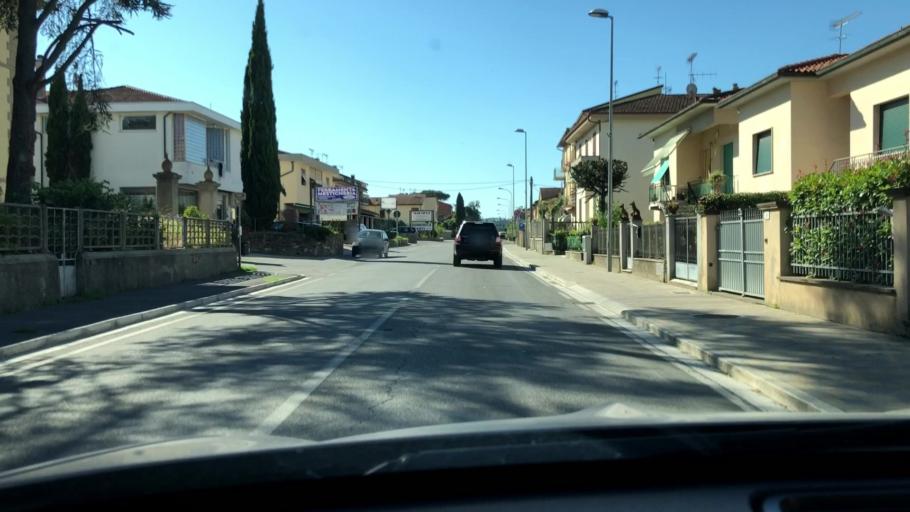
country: IT
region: Tuscany
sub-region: Province of Pisa
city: Forcoli
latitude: 43.6025
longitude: 10.7077
